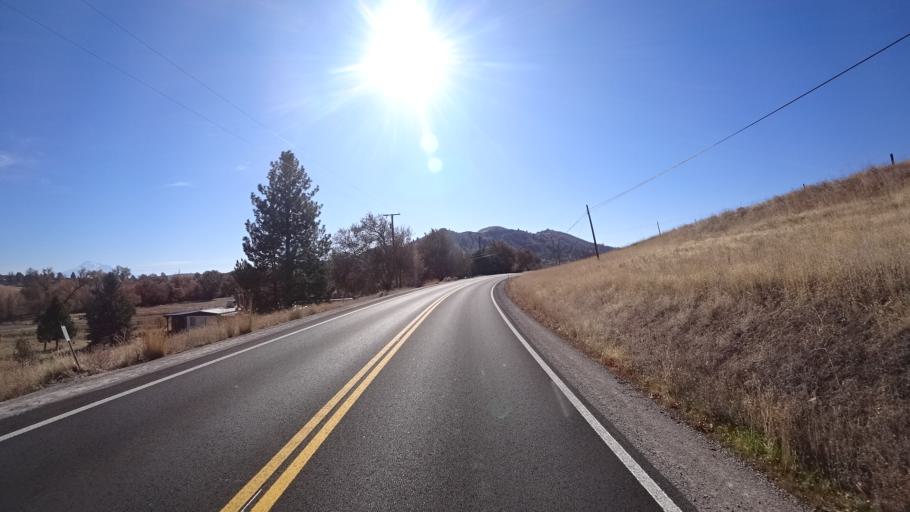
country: US
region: California
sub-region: Siskiyou County
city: Yreka
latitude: 41.7791
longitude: -122.5960
